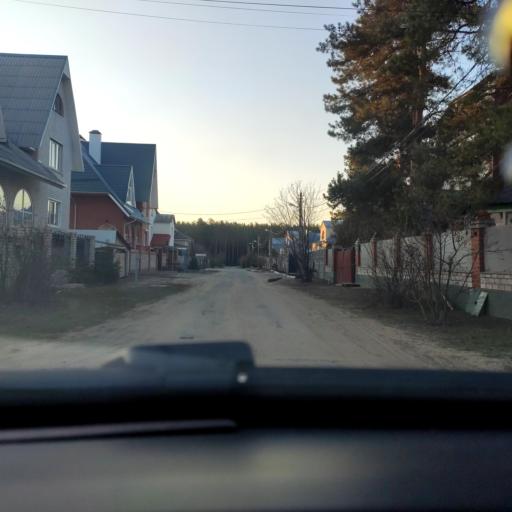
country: RU
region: Voronezj
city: Shilovo
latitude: 51.5779
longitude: 39.0440
